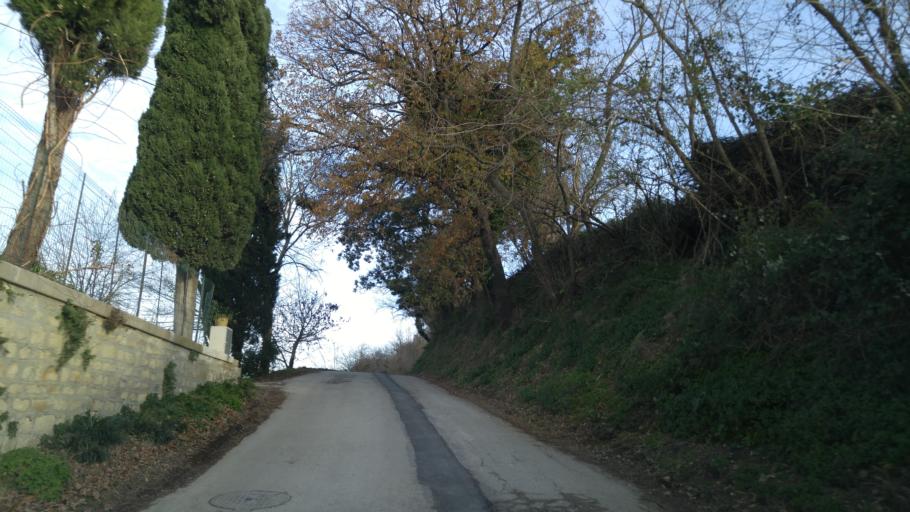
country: IT
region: The Marches
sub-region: Provincia di Pesaro e Urbino
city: Fenile
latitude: 43.8251
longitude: 12.9354
